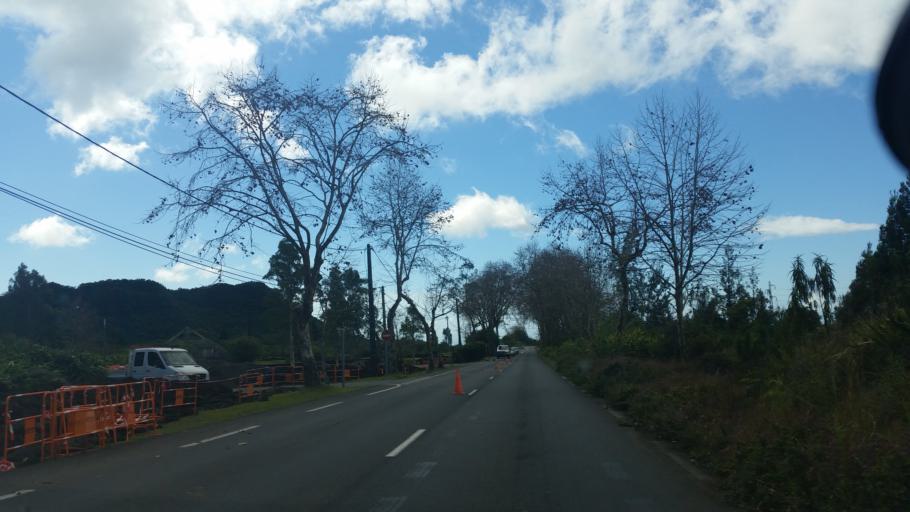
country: RE
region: Reunion
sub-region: Reunion
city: Saint-Benoit
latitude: -21.1193
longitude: 55.6445
